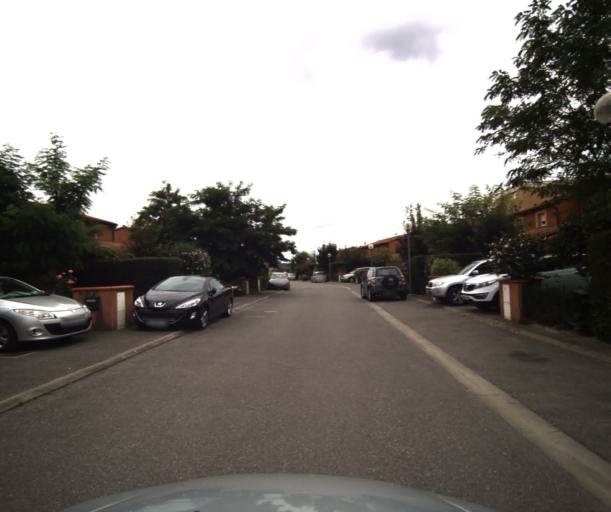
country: FR
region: Midi-Pyrenees
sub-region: Departement de la Haute-Garonne
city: Muret
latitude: 43.4518
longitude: 1.3232
